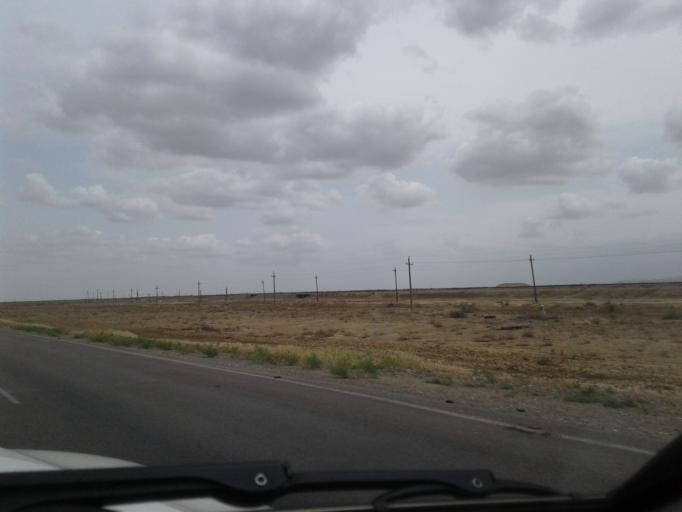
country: IR
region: Razavi Khorasan
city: Dargaz
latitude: 37.5911
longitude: 59.2429
